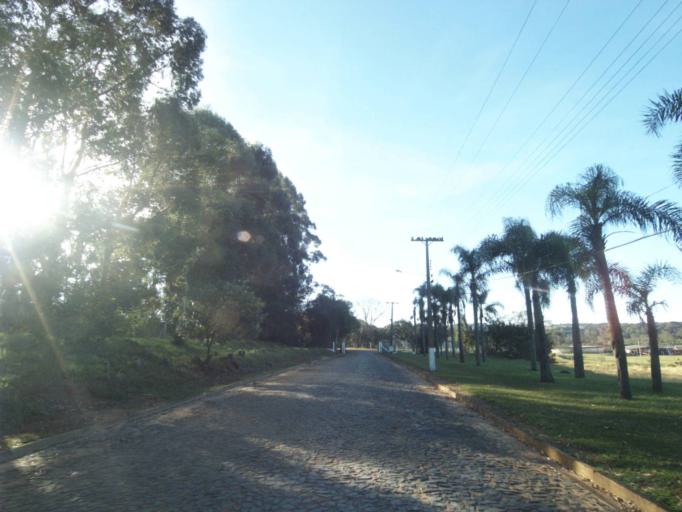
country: BR
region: Parana
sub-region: Tibagi
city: Tibagi
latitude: -24.5058
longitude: -50.4173
